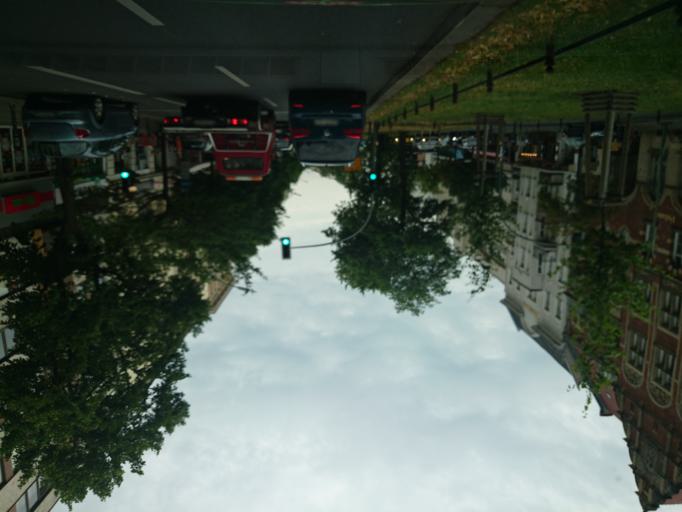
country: DE
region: Berlin
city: Berlin Schoeneberg
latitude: 52.4852
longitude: 13.3545
